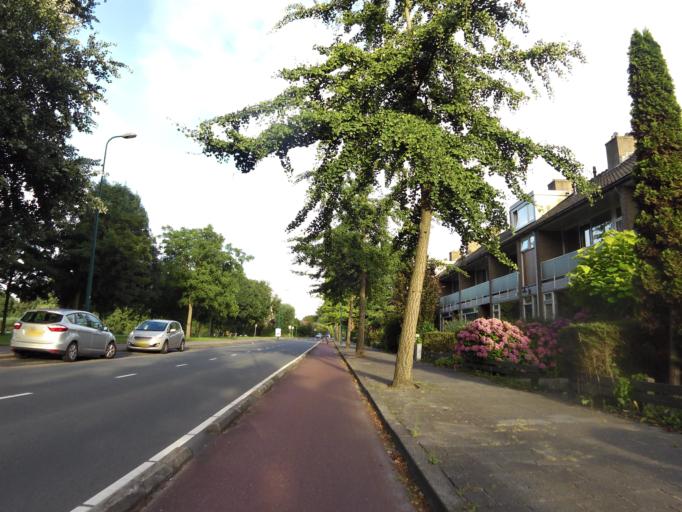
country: NL
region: South Holland
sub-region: Gemeente Oegstgeest
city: Oegstgeest
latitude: 52.1882
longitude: 4.4826
